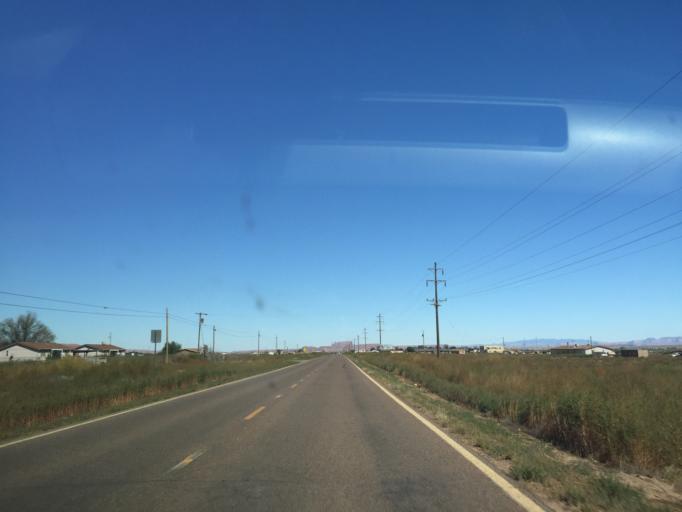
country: US
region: Arizona
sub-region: Apache County
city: Many Farms
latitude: 36.3406
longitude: -109.6231
